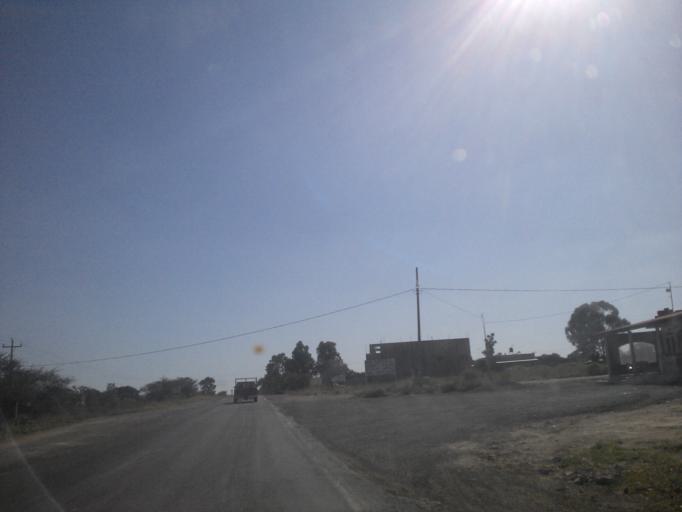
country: MX
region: Jalisco
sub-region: Arandas
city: Santiaguito (Santiaguito de Velazquez)
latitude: 20.7556
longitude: -102.2988
